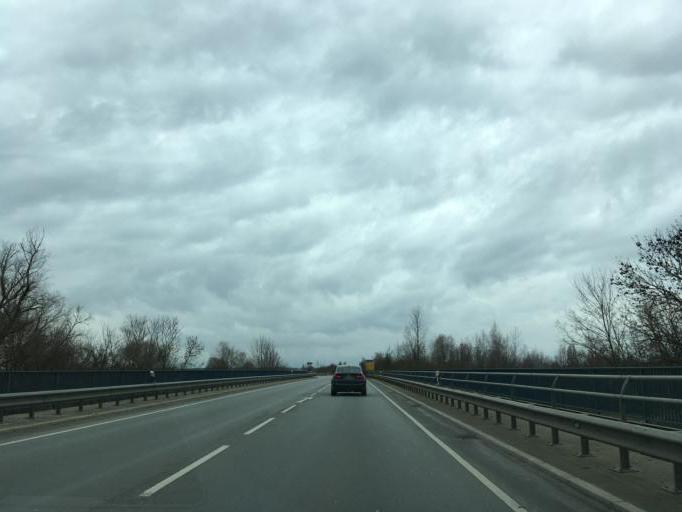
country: DE
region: Bavaria
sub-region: Lower Bavaria
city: Landau an der Isar
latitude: 48.6756
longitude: 12.6811
